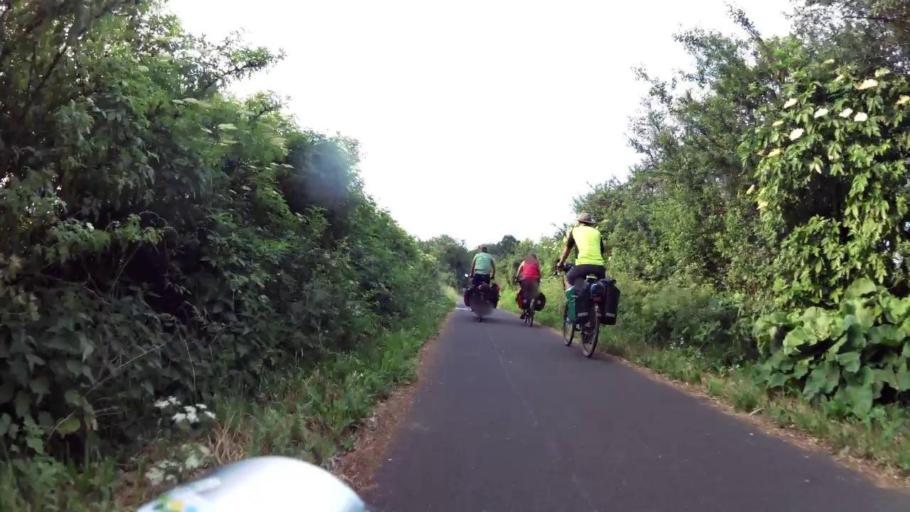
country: PL
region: Kujawsko-Pomorskie
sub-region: Powiat torunski
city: Lubianka
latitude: 53.1413
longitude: 18.4595
